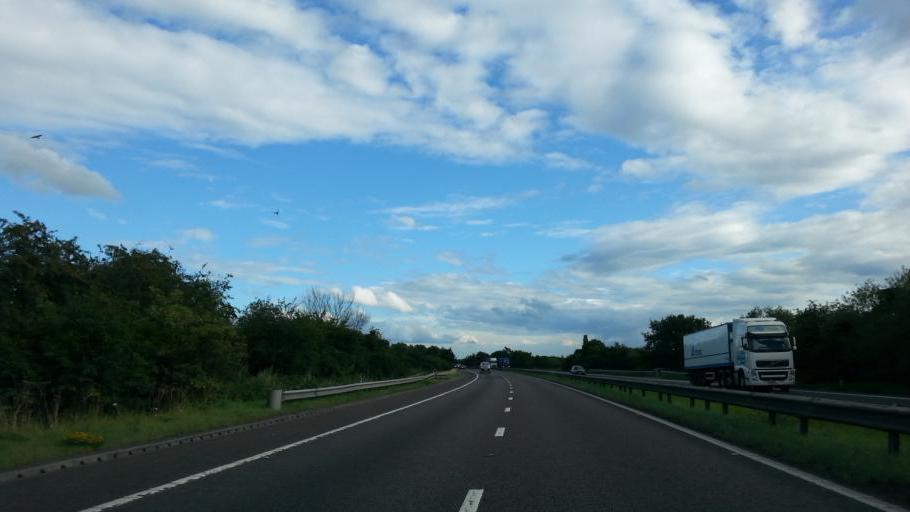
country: GB
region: England
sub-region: Doncaster
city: Tickhill
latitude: 53.4256
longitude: -1.0931
